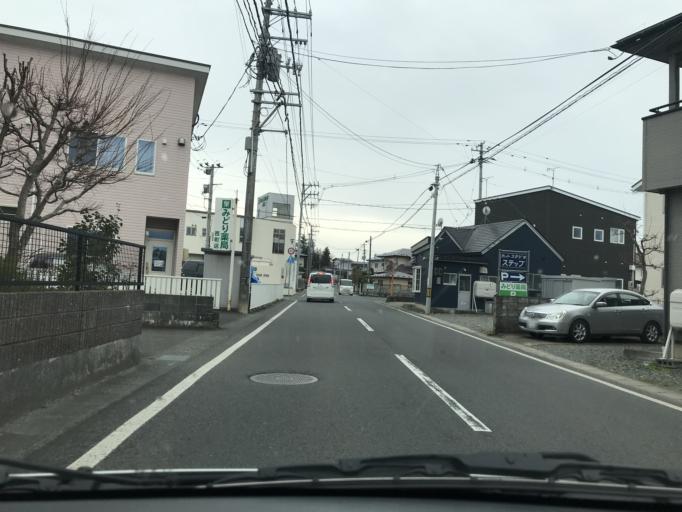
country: JP
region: Iwate
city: Mizusawa
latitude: 39.1378
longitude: 141.1328
